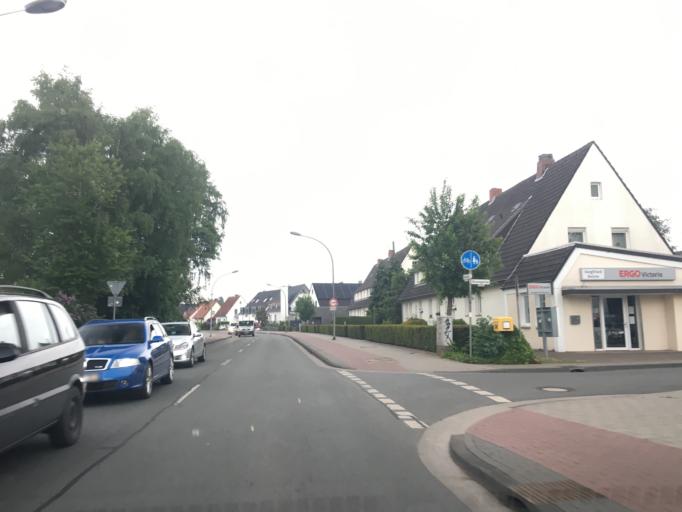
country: DE
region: North Rhine-Westphalia
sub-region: Regierungsbezirk Munster
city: Muenster
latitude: 51.9500
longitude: 7.6759
